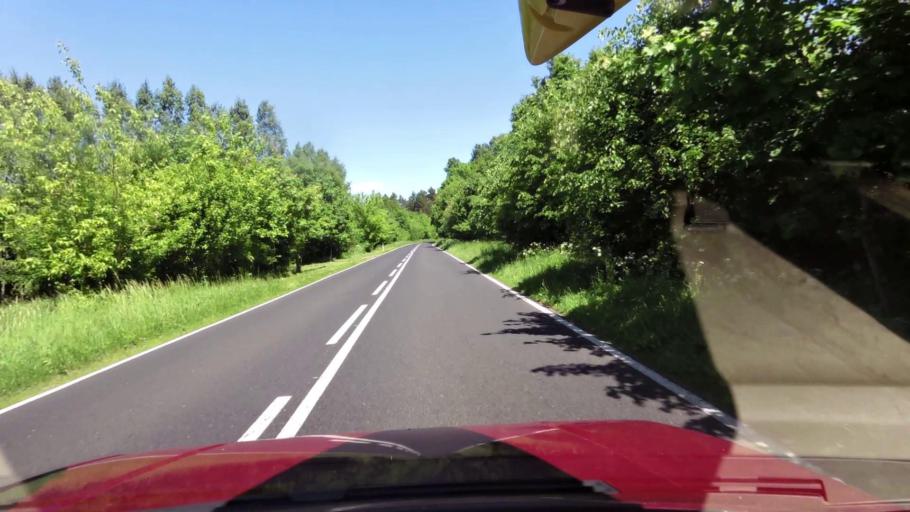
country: PL
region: West Pomeranian Voivodeship
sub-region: Powiat koszalinski
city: Polanow
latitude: 54.0116
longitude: 16.7185
